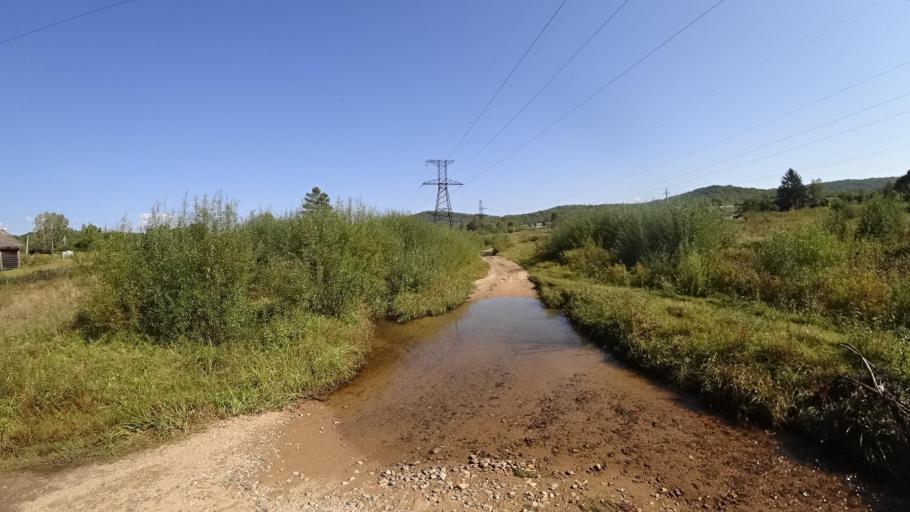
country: RU
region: Jewish Autonomous Oblast
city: Bira
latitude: 49.0014
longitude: 132.4766
